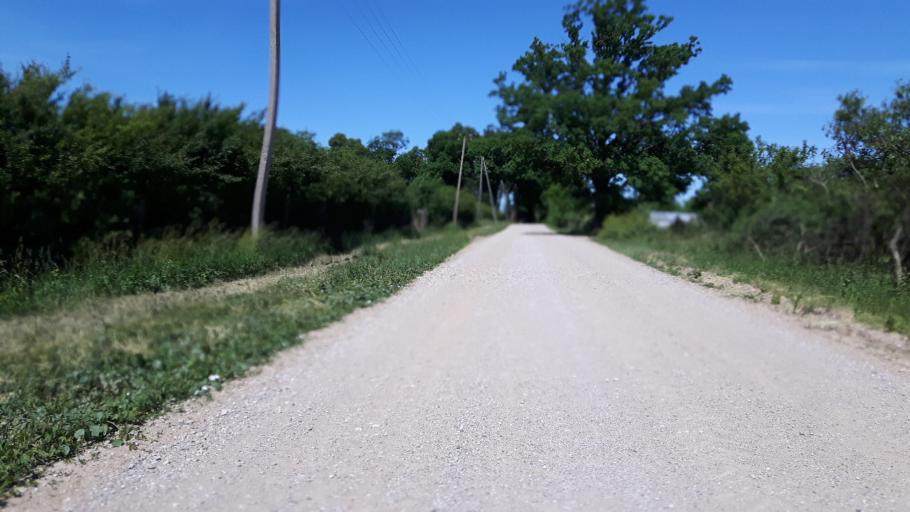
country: LV
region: Kandava
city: Kandava
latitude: 57.0424
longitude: 22.8792
